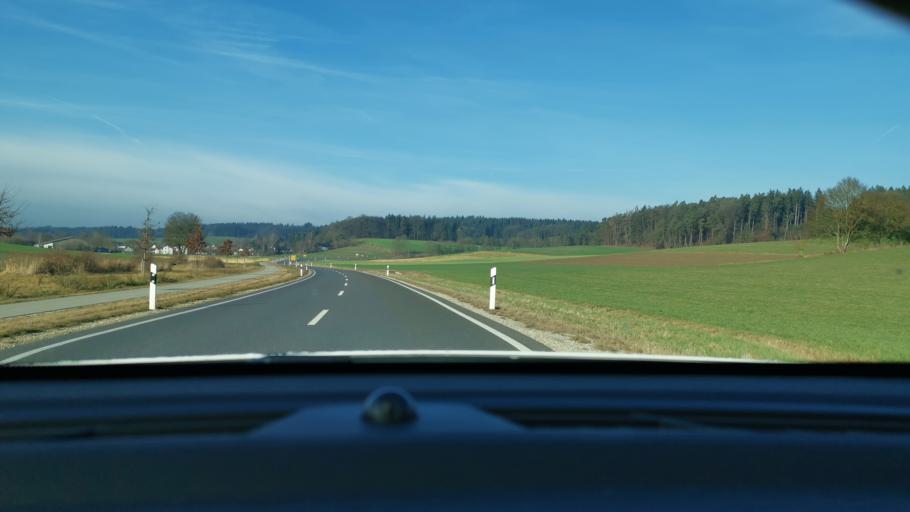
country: DE
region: Bavaria
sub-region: Swabia
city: Petersdorf
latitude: 48.5370
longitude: 11.0088
